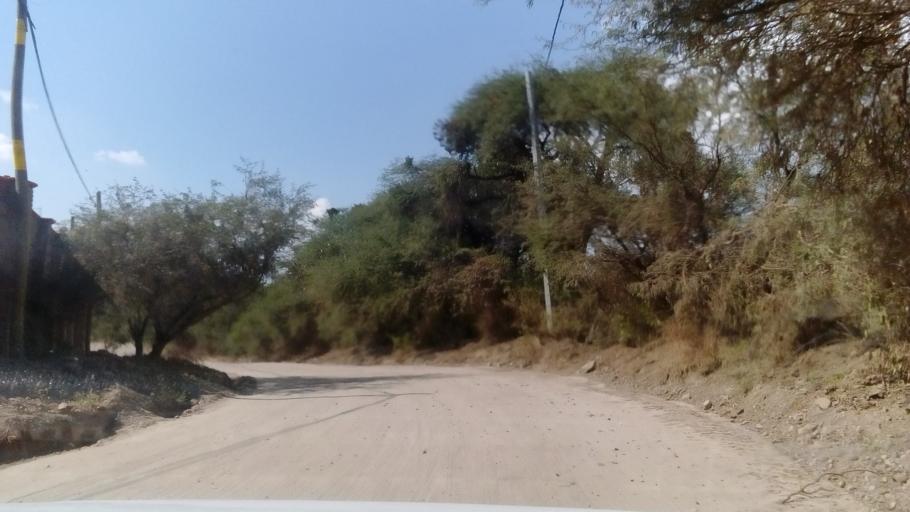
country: MX
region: Guanajuato
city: Duarte
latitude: 21.0794
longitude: -101.4994
